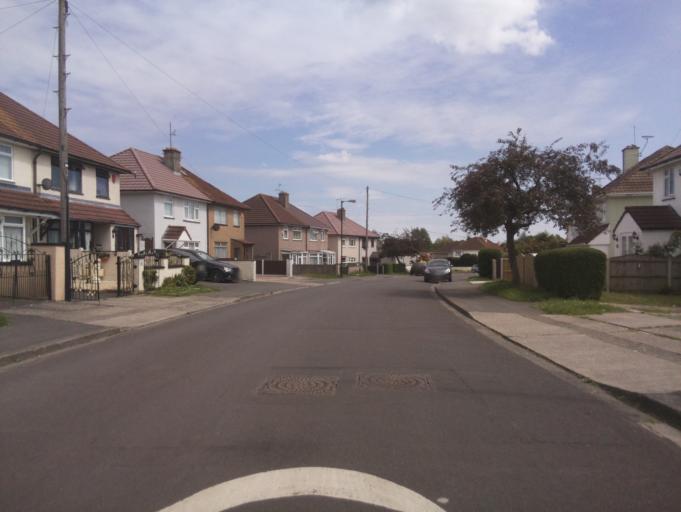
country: GB
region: England
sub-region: Bristol
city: Bristol
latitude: 51.5065
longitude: -2.6000
